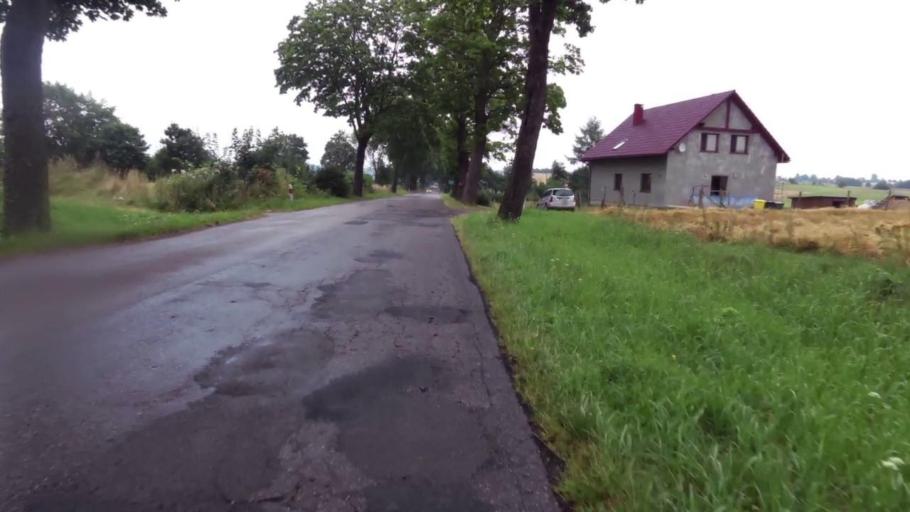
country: PL
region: West Pomeranian Voivodeship
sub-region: Powiat drawski
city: Czaplinek
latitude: 53.5987
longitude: 16.2518
